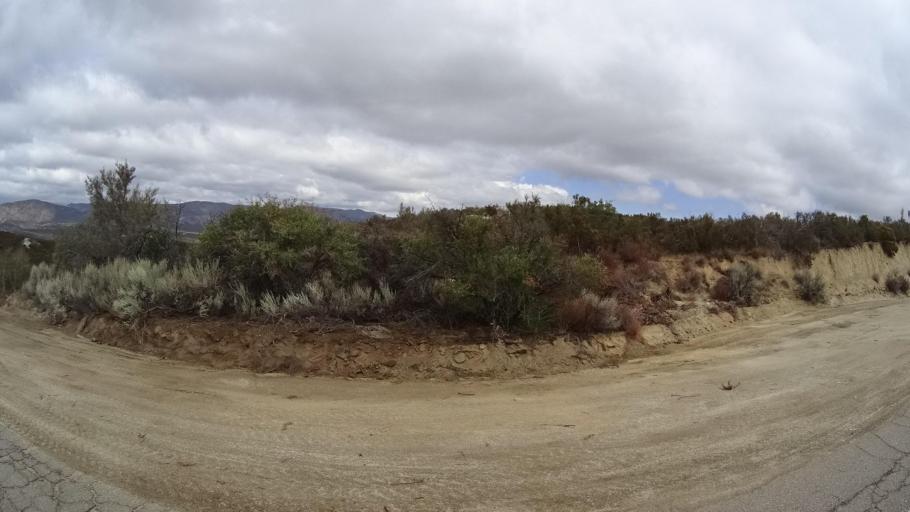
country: US
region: California
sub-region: San Diego County
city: Campo
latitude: 32.7197
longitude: -116.4047
